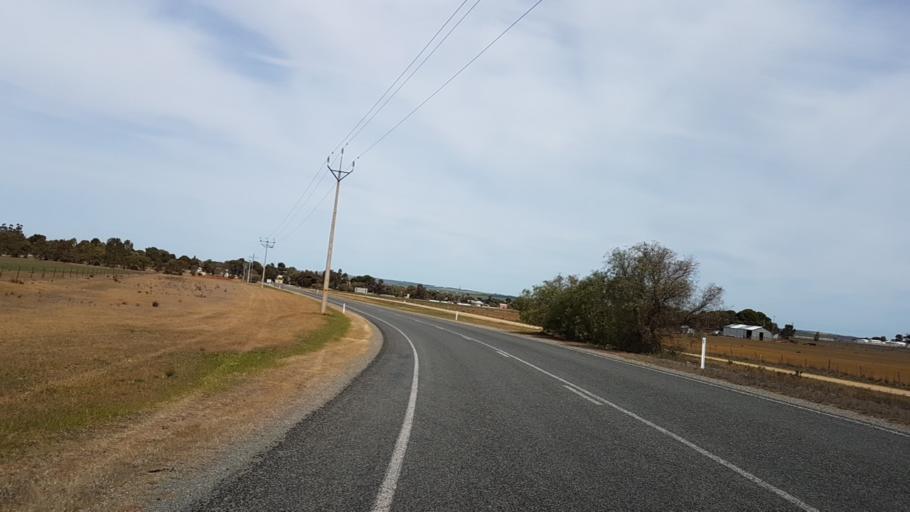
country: AU
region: South Australia
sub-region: Peterborough
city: Peterborough
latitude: -33.0223
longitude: 138.7506
